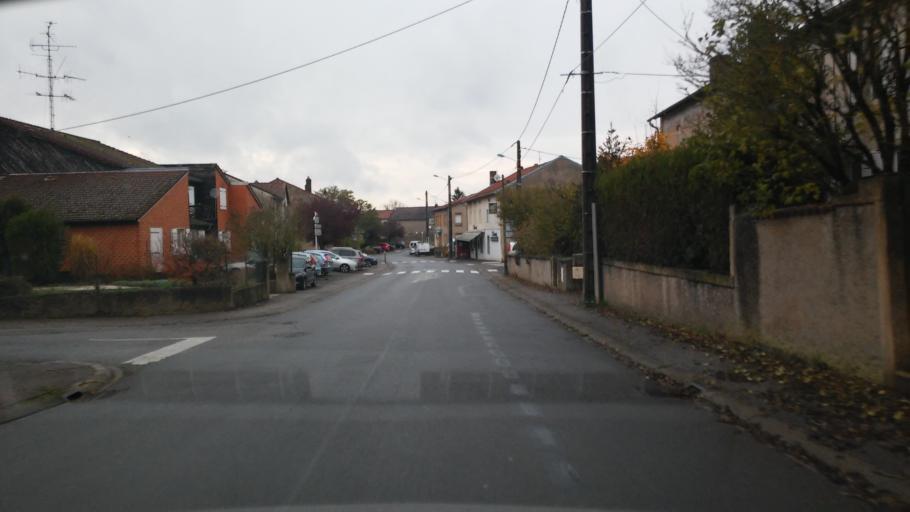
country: FR
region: Lorraine
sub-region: Departement de la Moselle
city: Vigy
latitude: 49.2016
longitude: 6.2991
